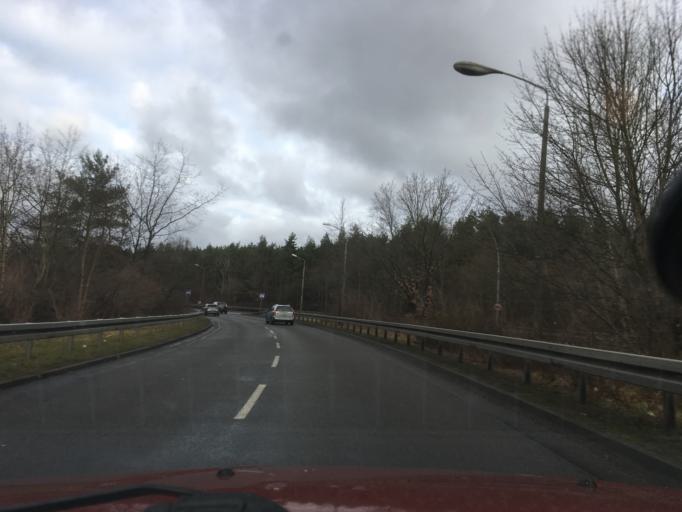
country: DE
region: Berlin
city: Grunau
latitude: 52.4171
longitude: 13.5695
